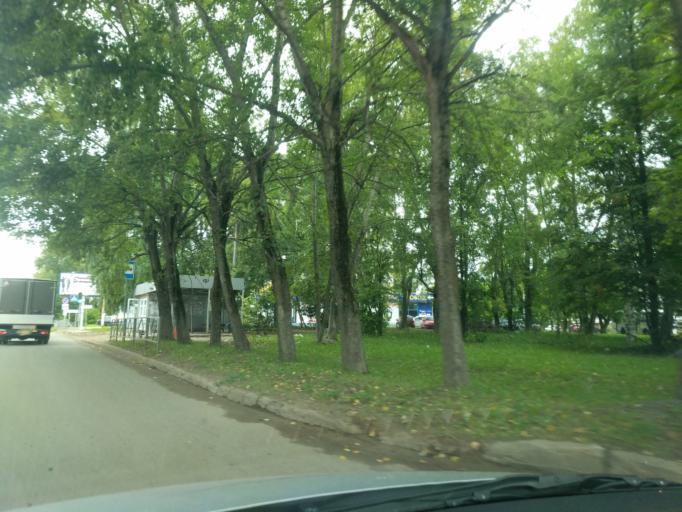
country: RU
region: Kirov
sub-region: Kirovo-Chepetskiy Rayon
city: Kirov
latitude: 58.6332
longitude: 49.6184
